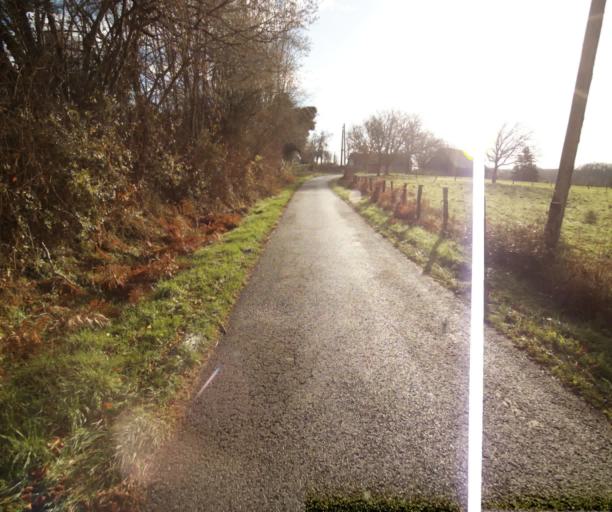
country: FR
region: Limousin
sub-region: Departement de la Correze
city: Sainte-Fereole
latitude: 45.2610
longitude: 1.6020
